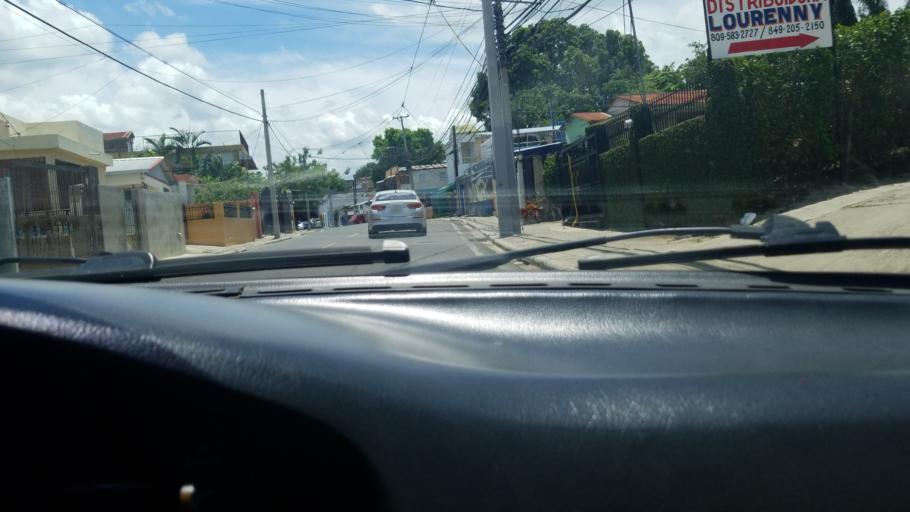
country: DO
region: Santiago
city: Santiago de los Caballeros
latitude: 19.4713
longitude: -70.6876
